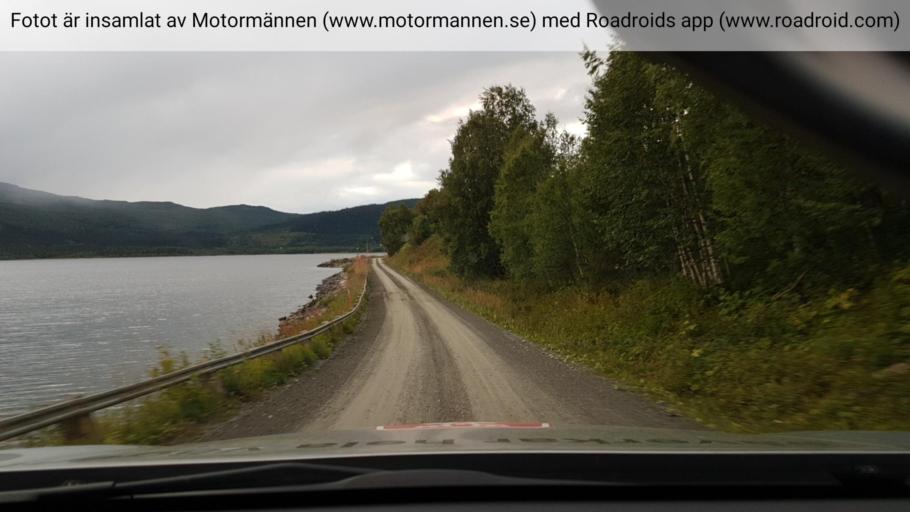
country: NO
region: Nordland
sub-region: Hattfjelldal
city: Hattfjelldal
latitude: 65.6501
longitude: 15.1769
